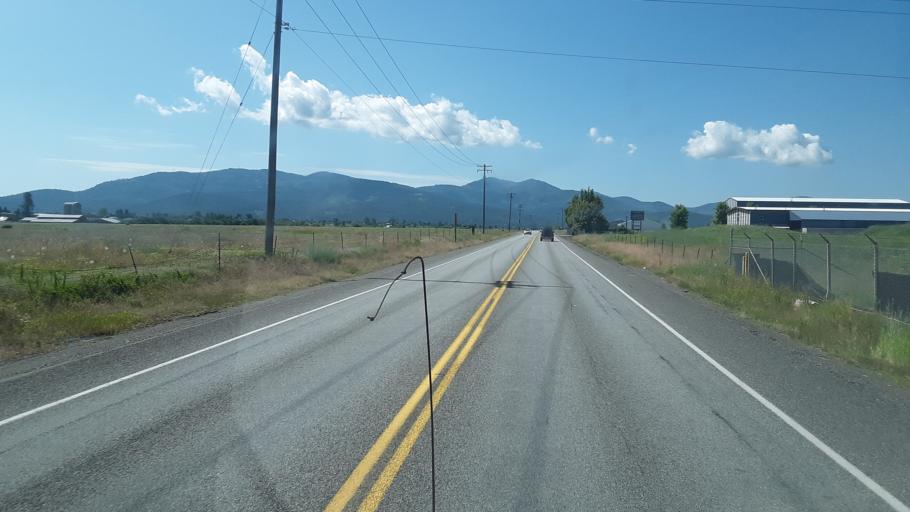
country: US
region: Idaho
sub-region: Kootenai County
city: Post Falls
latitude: 47.7426
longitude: -117.0020
